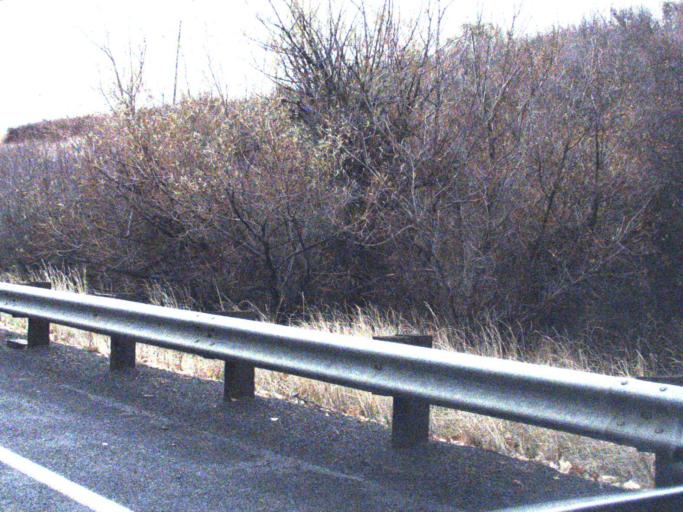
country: US
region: Washington
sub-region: Walla Walla County
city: Waitsburg
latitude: 46.1590
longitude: -118.1319
